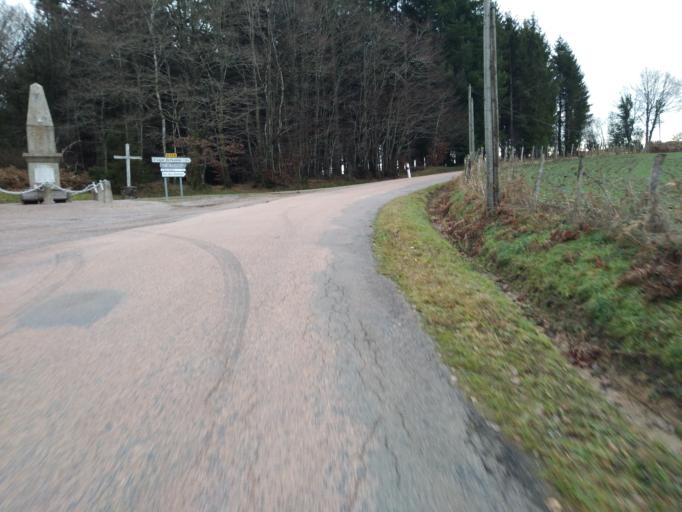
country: FR
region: Bourgogne
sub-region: Departement de la Cote-d'Or
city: Saulieu
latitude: 47.2753
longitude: 4.1598
